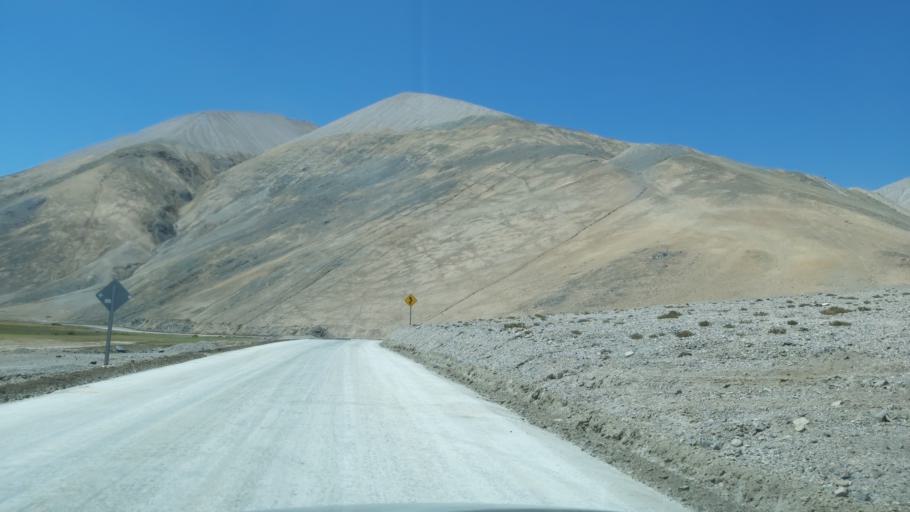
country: CL
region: Atacama
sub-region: Provincia de Chanaral
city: Diego de Almagro
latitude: -26.3963
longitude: -69.5126
